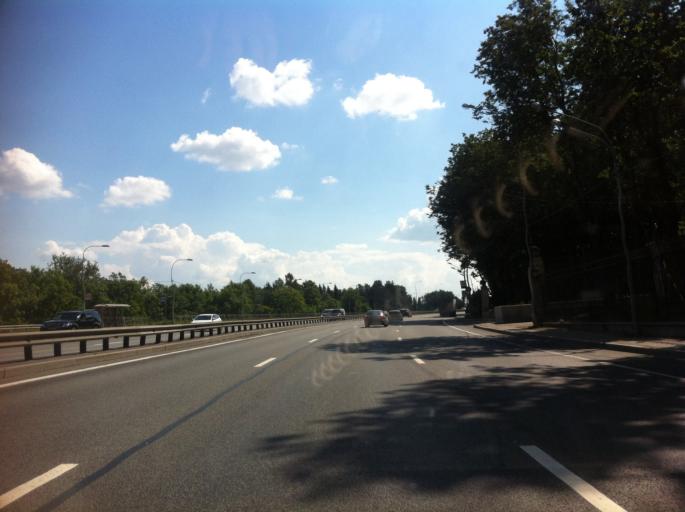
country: RU
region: St.-Petersburg
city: Aleksandrovskaya
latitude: 59.7714
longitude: 30.3323
